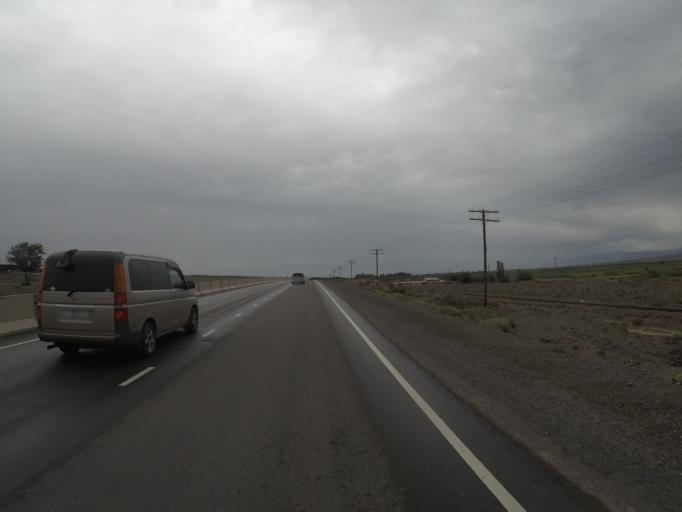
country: KG
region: Ysyk-Koel
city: Balykchy
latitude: 42.4592
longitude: 76.0864
